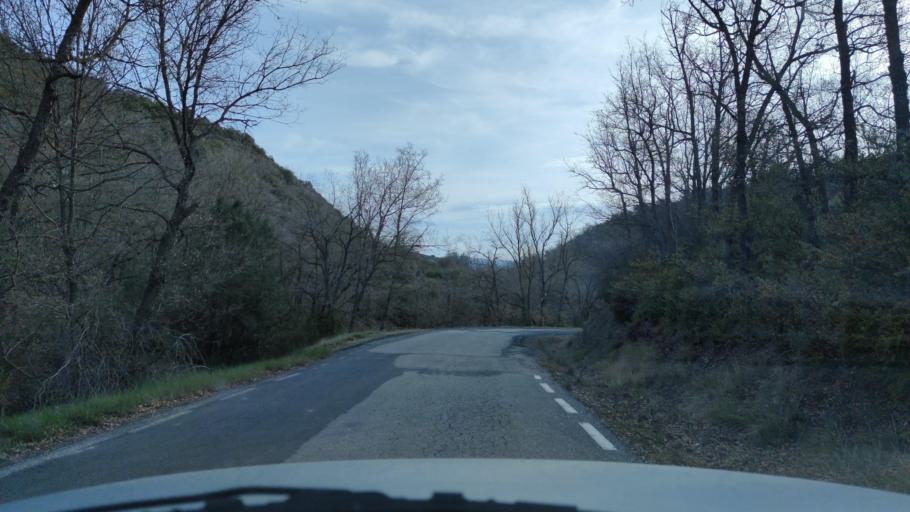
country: ES
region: Catalonia
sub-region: Provincia de Lleida
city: Os de Balaguer
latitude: 41.8869
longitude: 0.7910
